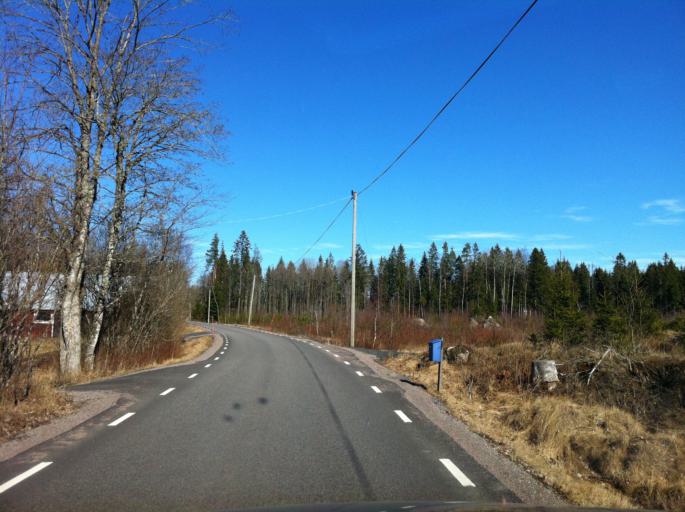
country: SE
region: Vaestra Goetaland
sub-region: Toreboda Kommun
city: Toereboda
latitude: 58.7580
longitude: 14.0990
